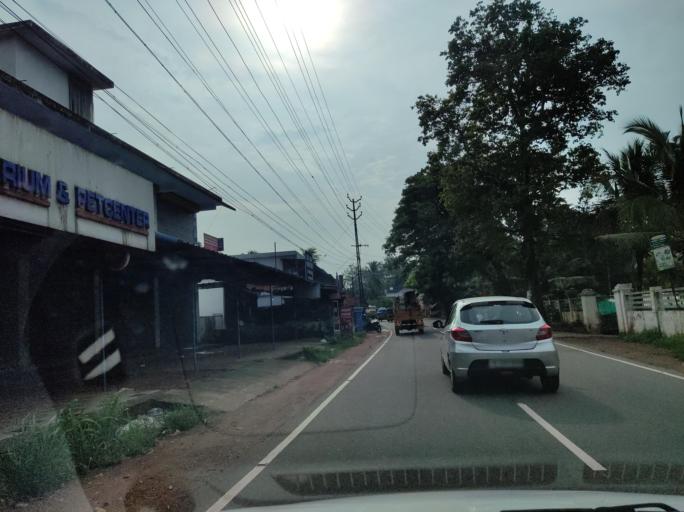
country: IN
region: Kerala
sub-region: Alappuzha
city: Kattanam
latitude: 9.1733
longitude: 76.5895
